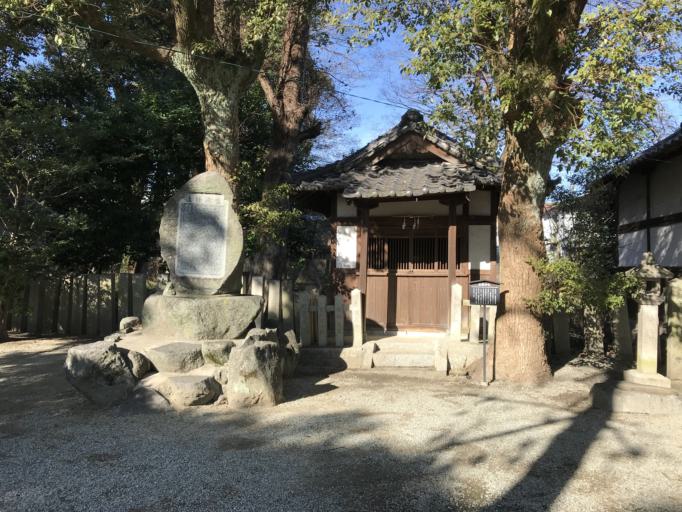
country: JP
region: Nara
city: Kashihara-shi
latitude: 34.5159
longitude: 135.7469
